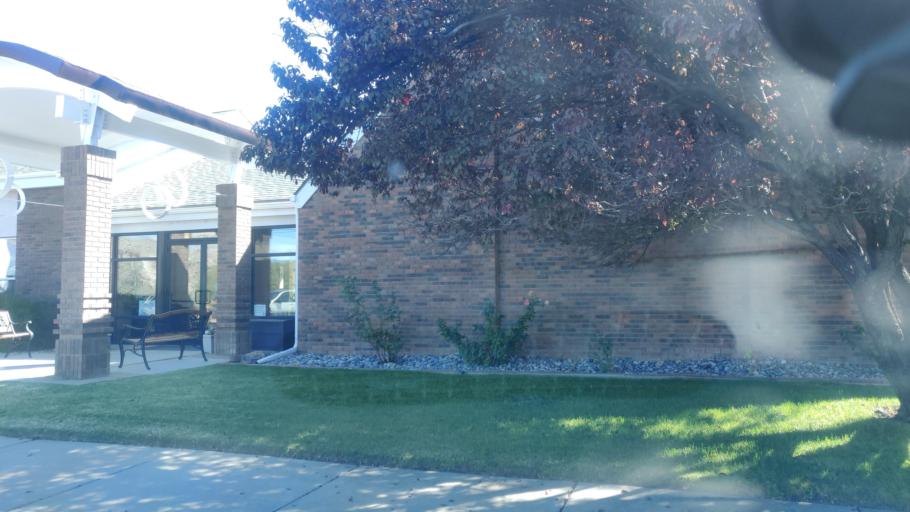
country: US
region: Colorado
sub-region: Mesa County
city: Redlands
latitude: 39.0700
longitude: -108.6435
